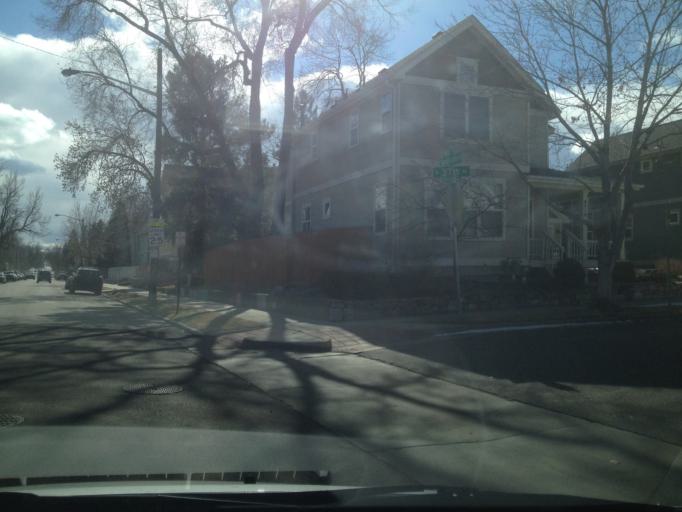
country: US
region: Colorado
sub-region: Jefferson County
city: Edgewater
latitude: 39.7676
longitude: -105.0441
